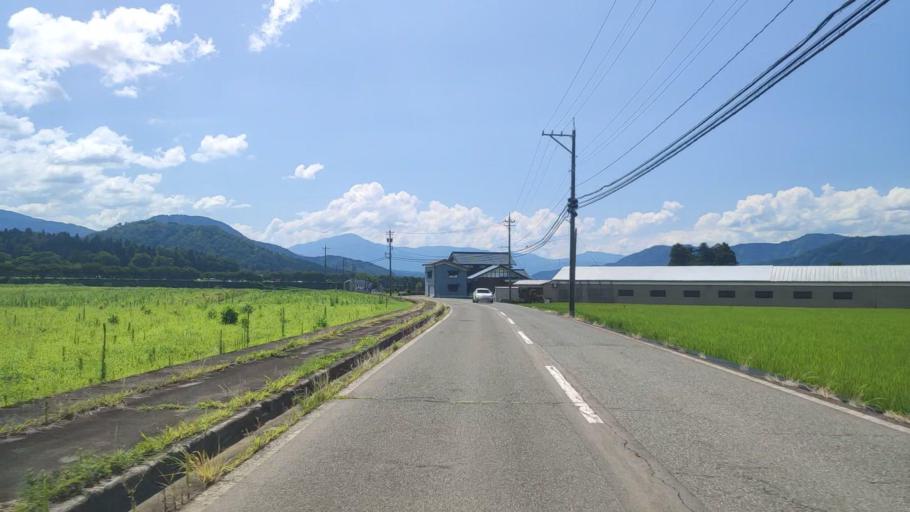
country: JP
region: Fukui
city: Katsuyama
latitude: 36.0880
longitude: 136.4930
